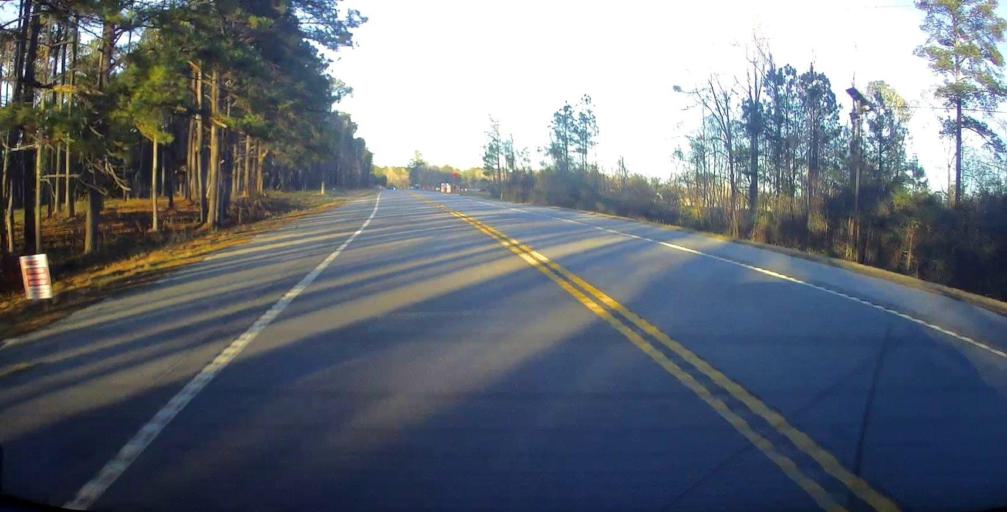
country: US
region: Georgia
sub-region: Harris County
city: Hamilton
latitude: 32.6641
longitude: -84.9774
